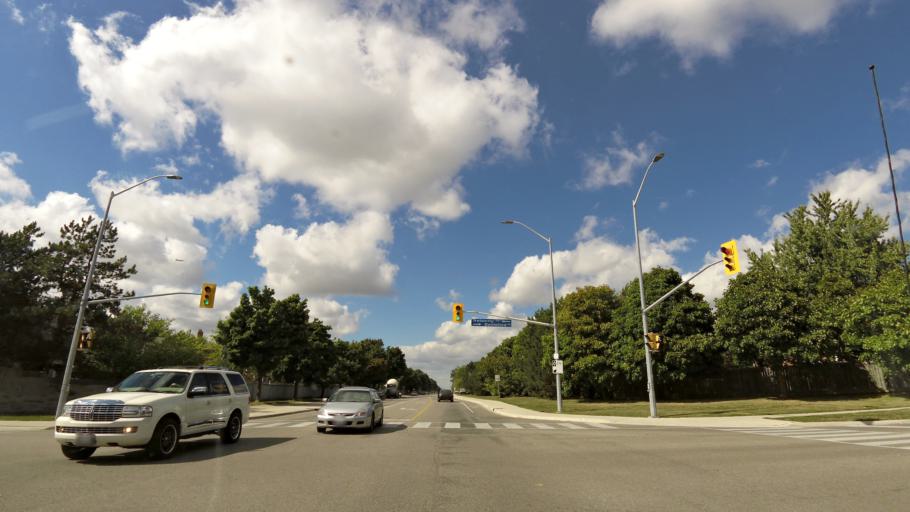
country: CA
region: Ontario
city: Mississauga
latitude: 43.5740
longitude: -79.7626
